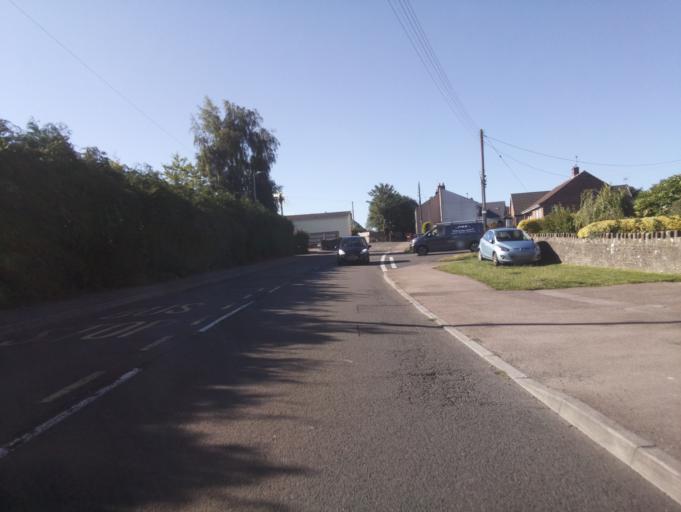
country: GB
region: England
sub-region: Gloucestershire
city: Coleford
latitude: 51.7940
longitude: -2.5980
